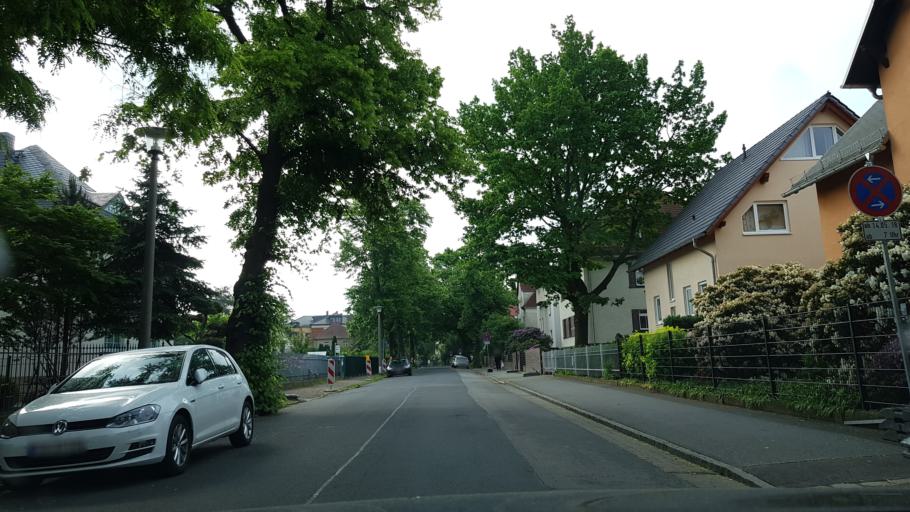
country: DE
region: Saxony
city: Heidenau
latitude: 51.0213
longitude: 13.8344
